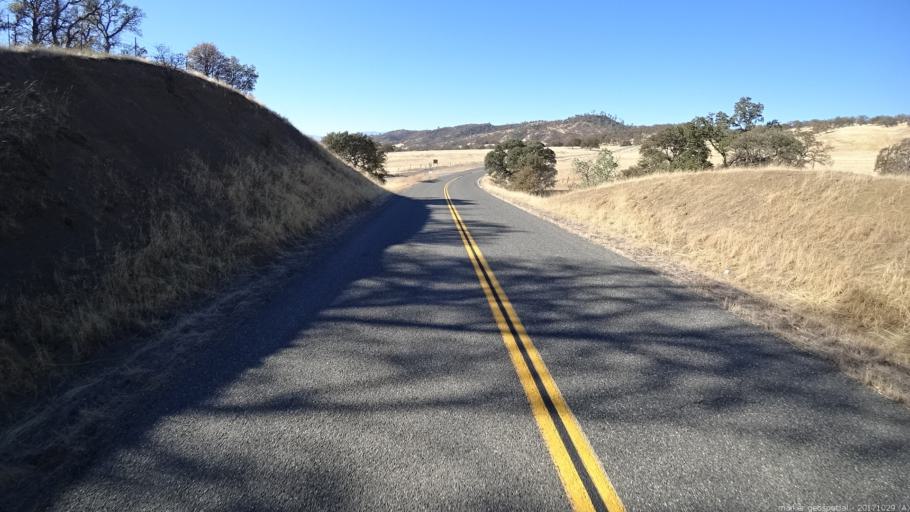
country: US
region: California
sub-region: Shasta County
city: Shasta
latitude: 40.4399
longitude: -122.6600
